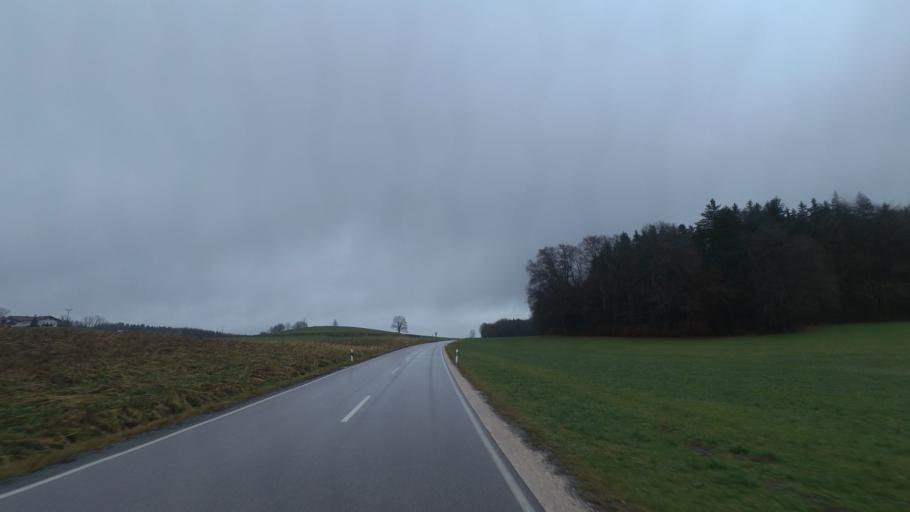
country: DE
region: Bavaria
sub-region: Upper Bavaria
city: Sankt Leonhard am Wonneberg
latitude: 47.9283
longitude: 12.6616
